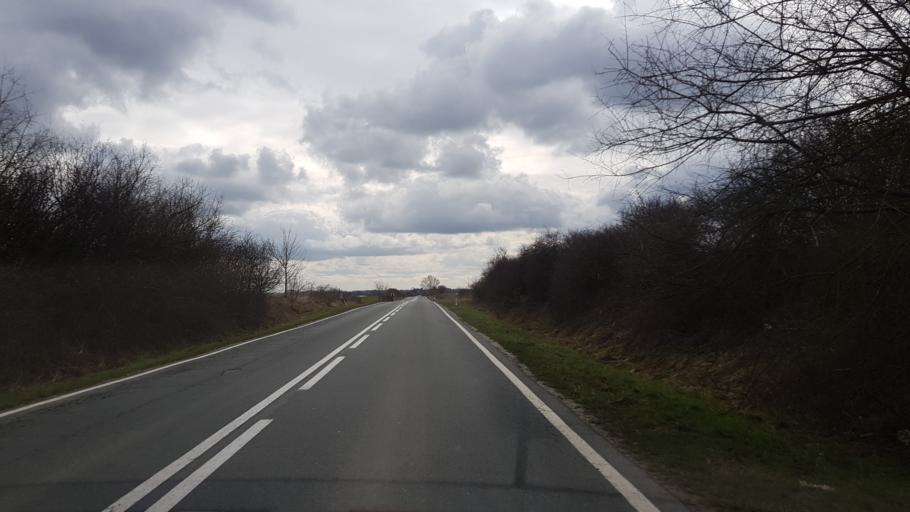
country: PL
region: West Pomeranian Voivodeship
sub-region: Powiat gryfinski
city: Banie
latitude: 53.1479
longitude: 14.6072
